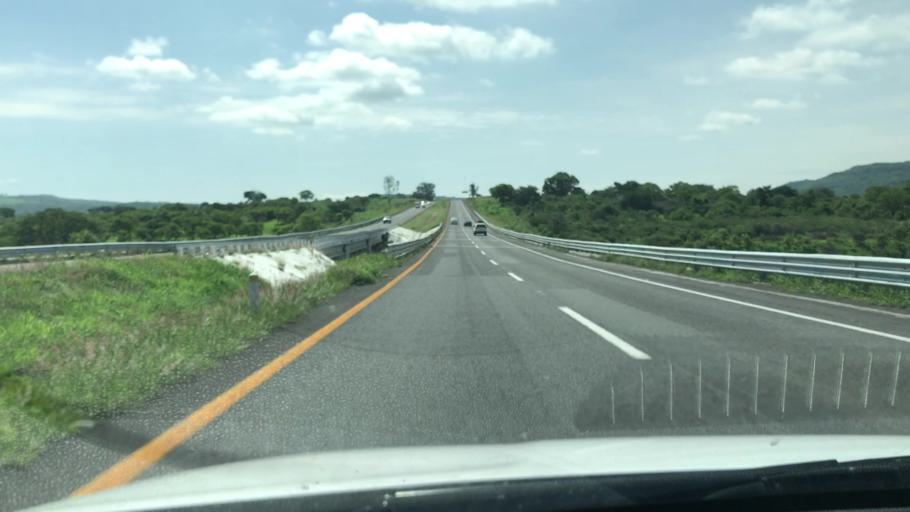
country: MX
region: Jalisco
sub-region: Zapotlanejo
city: La Mezquitera
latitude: 20.5514
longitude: -103.0461
